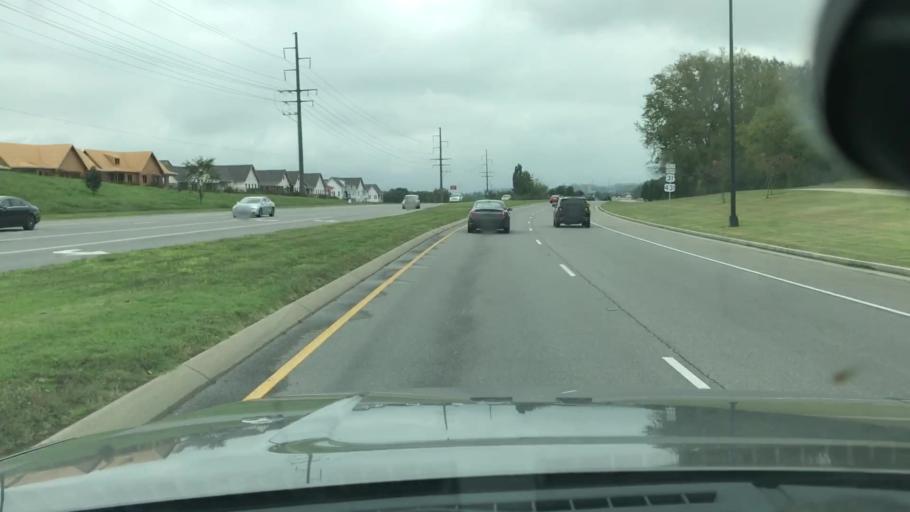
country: US
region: Tennessee
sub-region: Williamson County
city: Franklin
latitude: 35.9466
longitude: -86.8512
